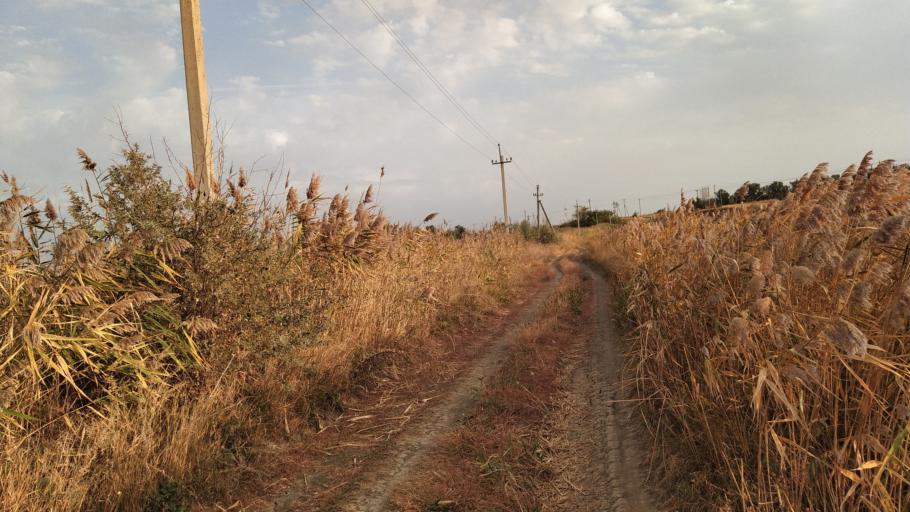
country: RU
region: Rostov
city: Kuleshovka
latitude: 47.1108
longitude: 39.6113
